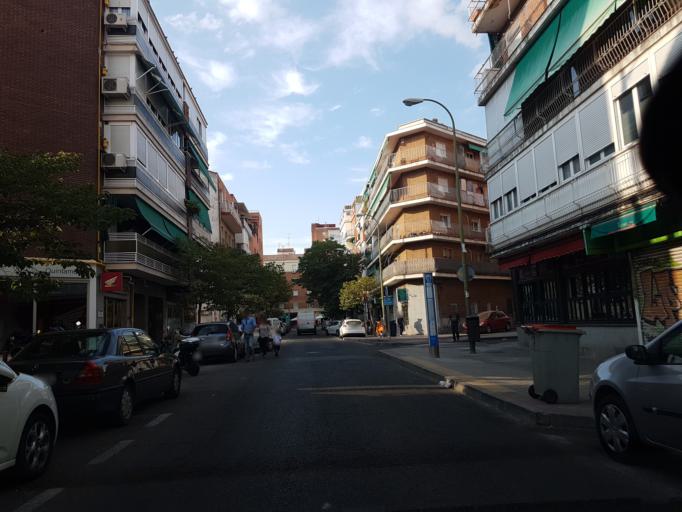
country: ES
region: Madrid
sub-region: Provincia de Madrid
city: Moratalaz
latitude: 40.4320
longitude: -3.6492
